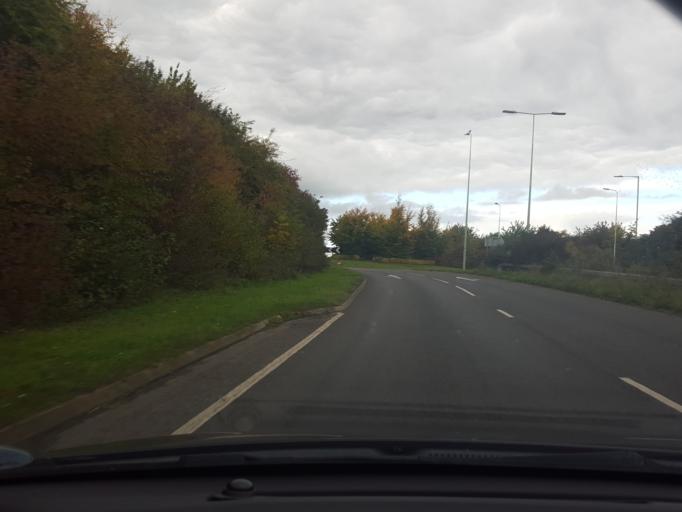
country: GB
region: England
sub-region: Suffolk
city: Bury St Edmunds
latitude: 52.2636
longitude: 0.7252
